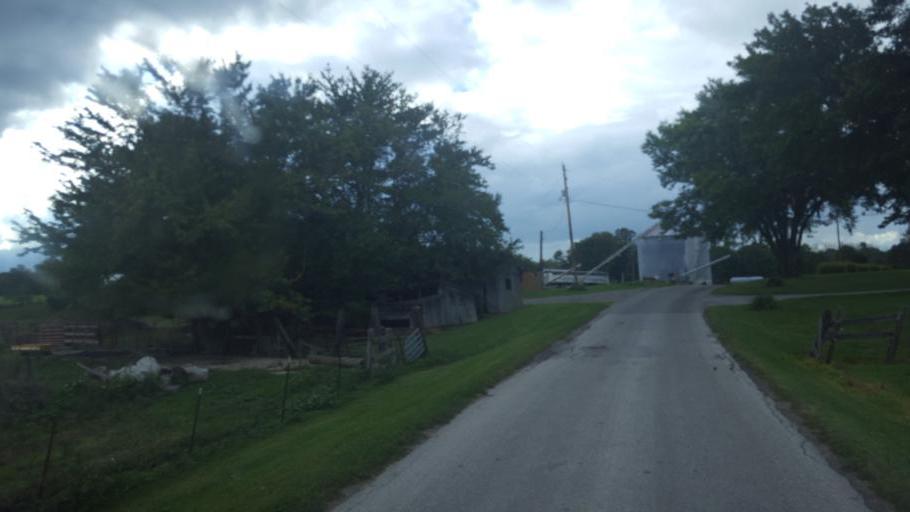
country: US
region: Ohio
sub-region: Jackson County
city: Oak Hill
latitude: 38.9403
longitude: -82.6276
